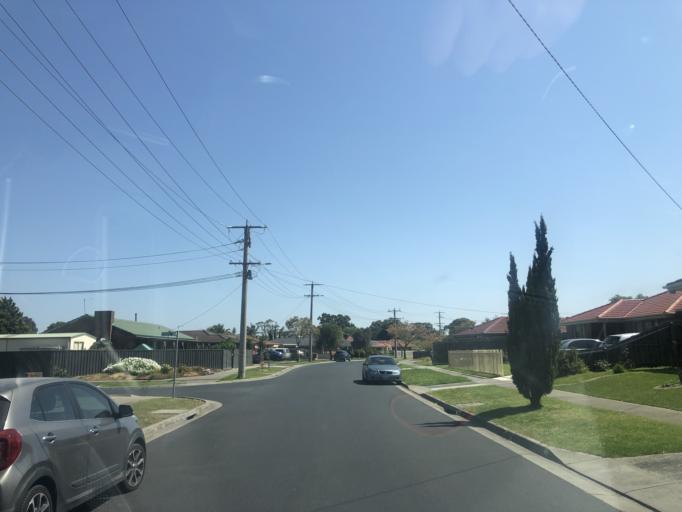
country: AU
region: Victoria
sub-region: Casey
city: Hallam
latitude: -38.0351
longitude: 145.2740
